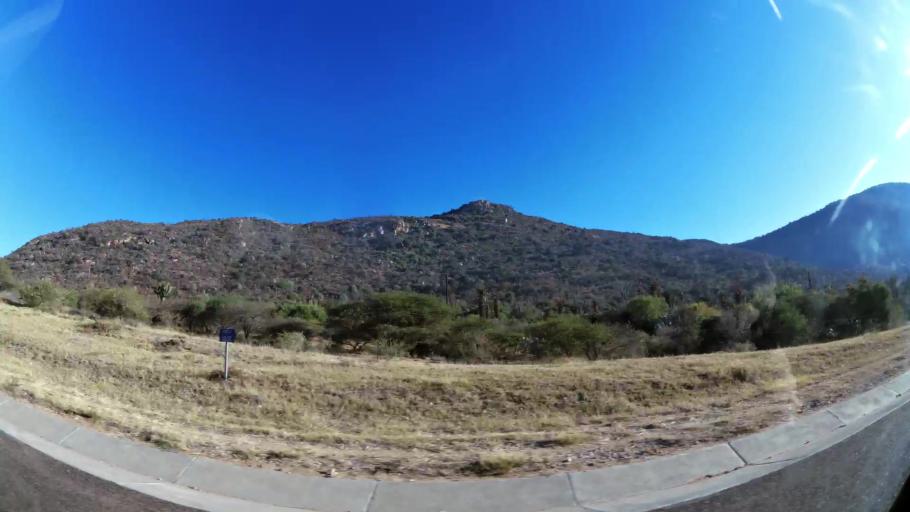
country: ZA
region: Limpopo
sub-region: Capricorn District Municipality
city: Mankoeng
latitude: -23.9430
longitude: 29.8073
